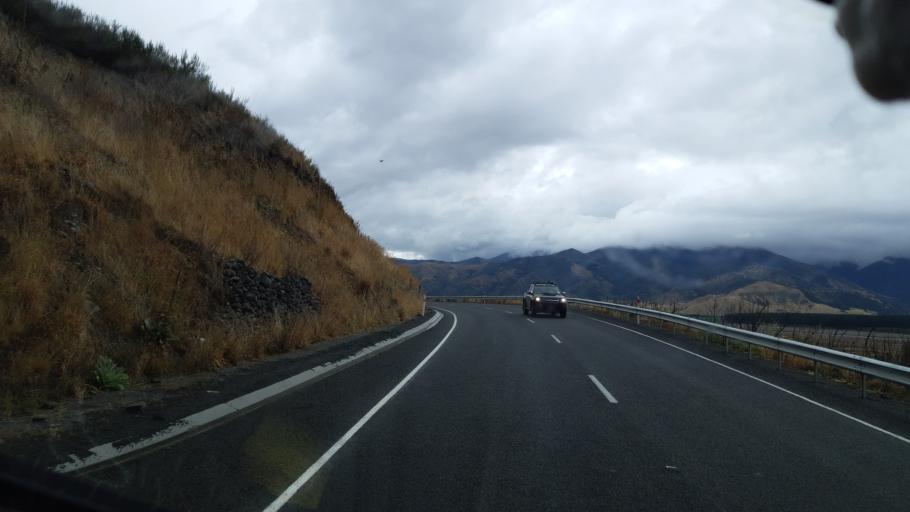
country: NZ
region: Canterbury
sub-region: Hurunui District
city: Amberley
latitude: -42.5769
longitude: 172.7339
